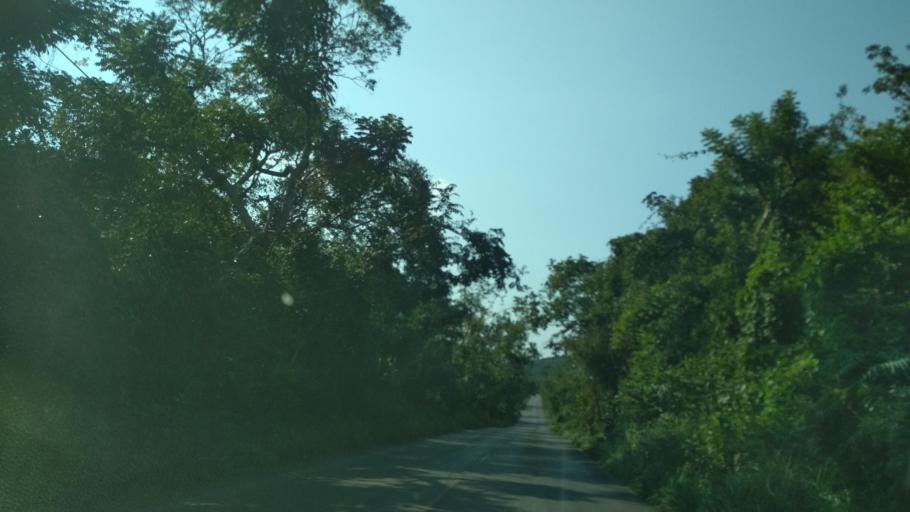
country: MX
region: Veracruz
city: Agua Dulce
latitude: 20.3999
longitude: -97.2163
